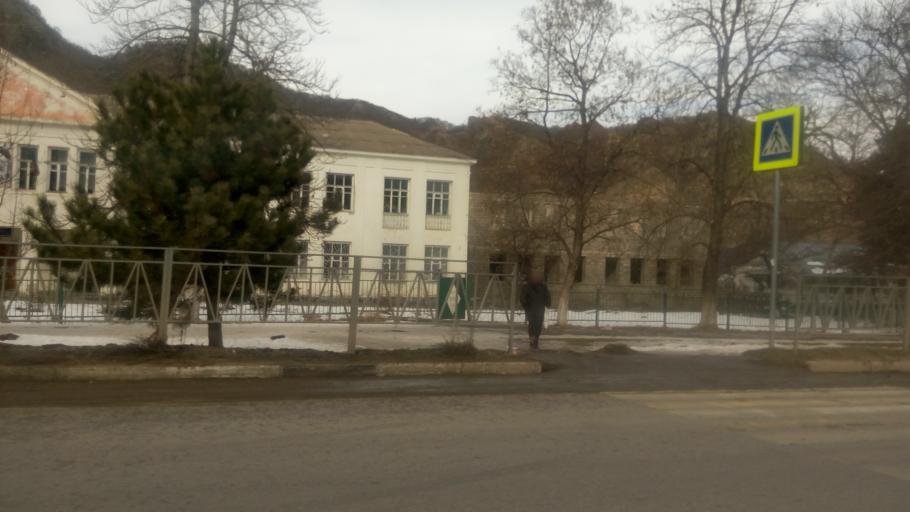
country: RU
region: Karachayevo-Cherkesiya
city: Karachayevsk
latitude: 43.7687
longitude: 41.9029
